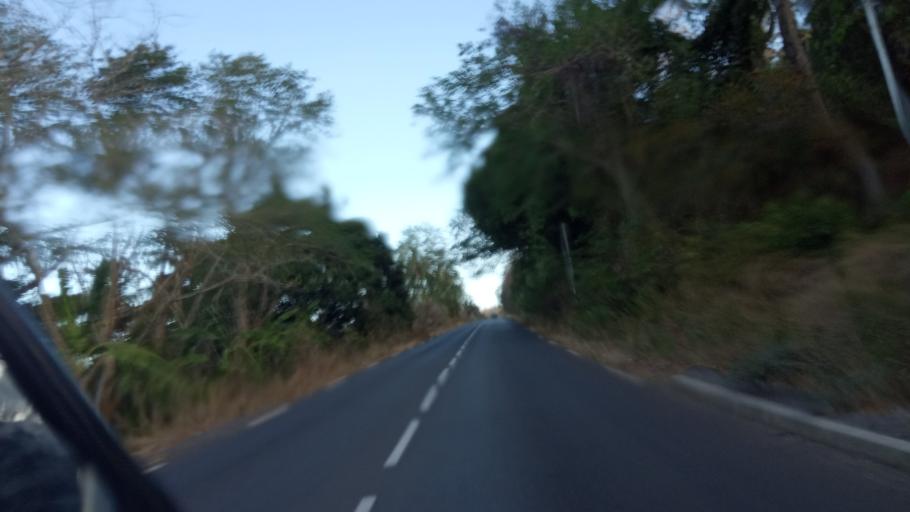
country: YT
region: Dembeni
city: Dembeni
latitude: -12.8519
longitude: 45.1949
